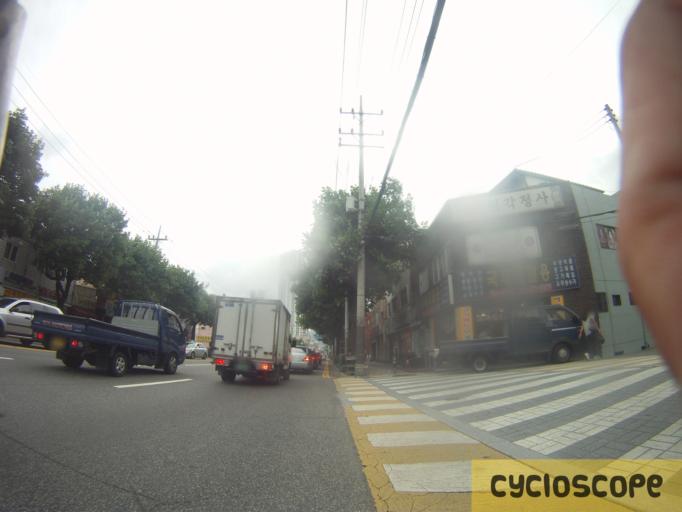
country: KR
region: Busan
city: Busan
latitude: 35.1751
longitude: 129.0851
